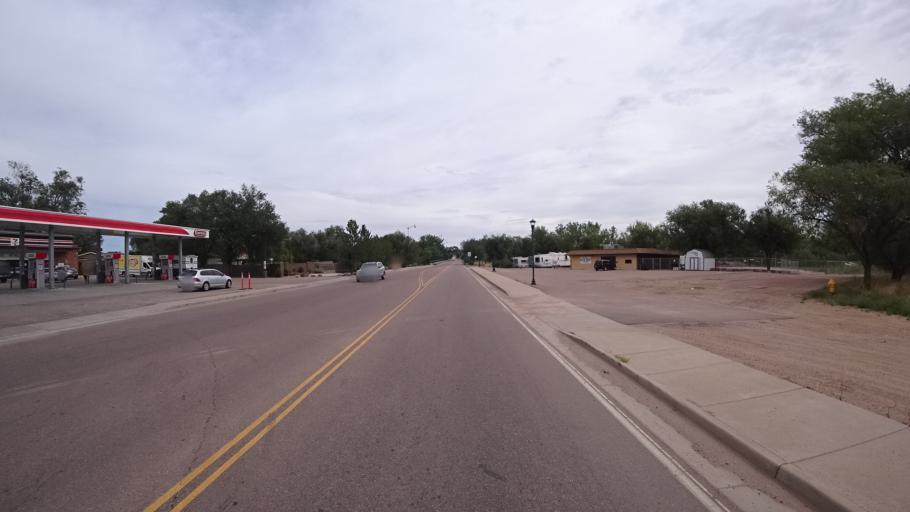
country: US
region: Colorado
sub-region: El Paso County
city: Fountain
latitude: 38.6759
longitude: -104.7058
